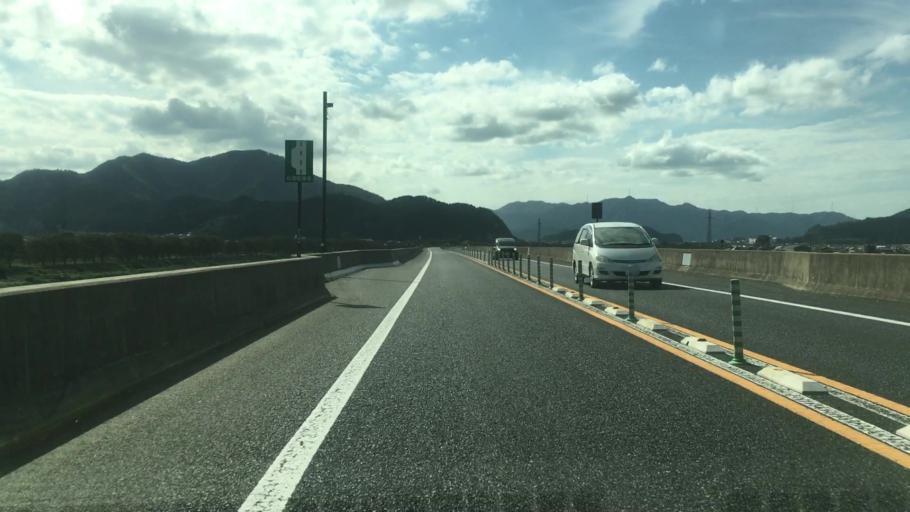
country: JP
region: Kyoto
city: Fukuchiyama
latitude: 35.1984
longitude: 135.0424
